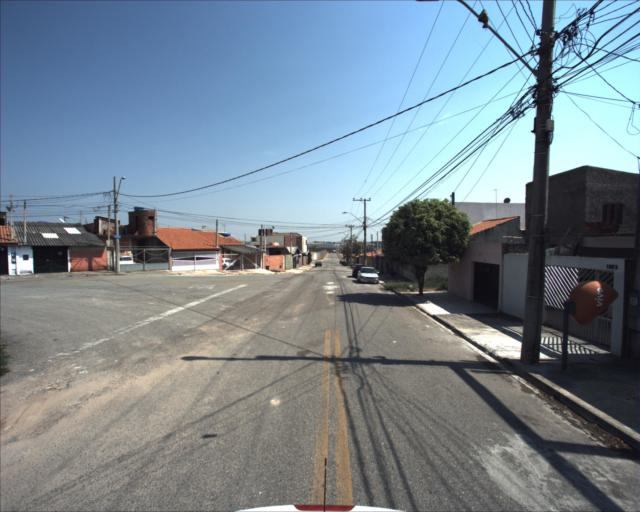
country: BR
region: Sao Paulo
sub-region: Sorocaba
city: Sorocaba
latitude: -23.4347
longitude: -47.4875
